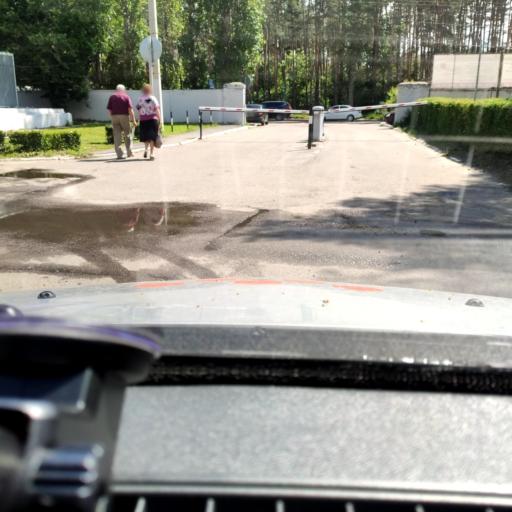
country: RU
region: Voronezj
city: Somovo
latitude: 51.6870
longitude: 39.2855
